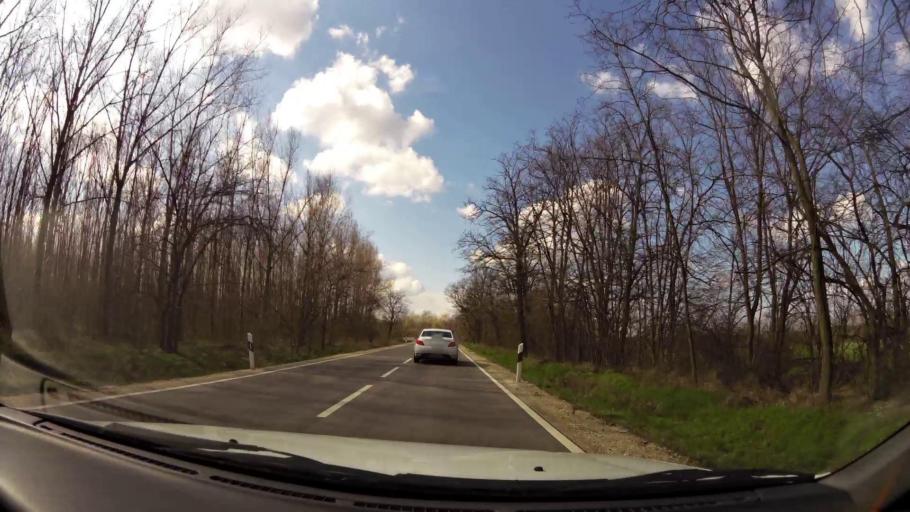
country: HU
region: Pest
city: Forropuszta
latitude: 47.4633
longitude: 19.6522
